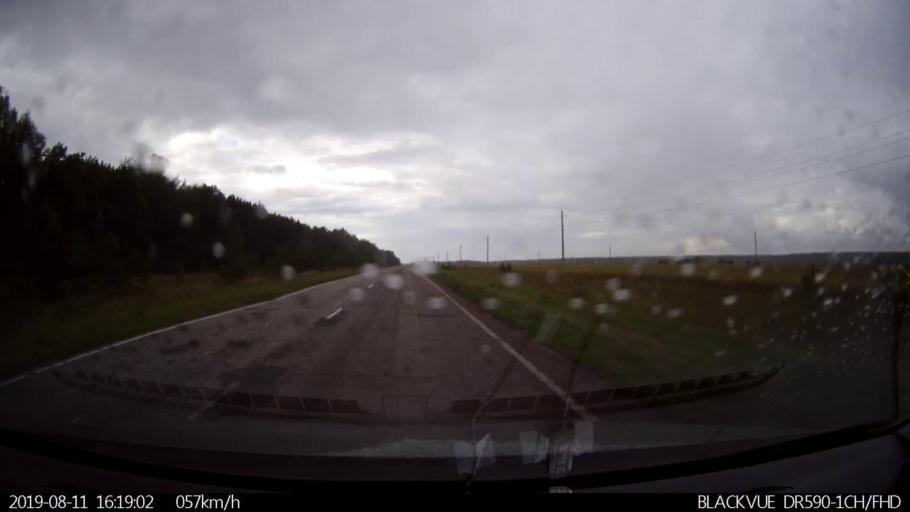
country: RU
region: Ulyanovsk
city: Mayna
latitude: 54.0606
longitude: 47.6088
